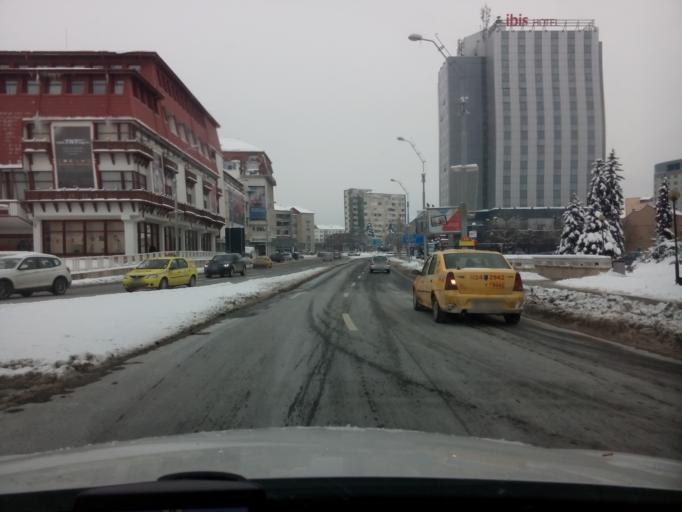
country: RO
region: Sibiu
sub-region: Municipiul Sibiu
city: Sibiu
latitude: 45.7908
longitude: 24.1485
